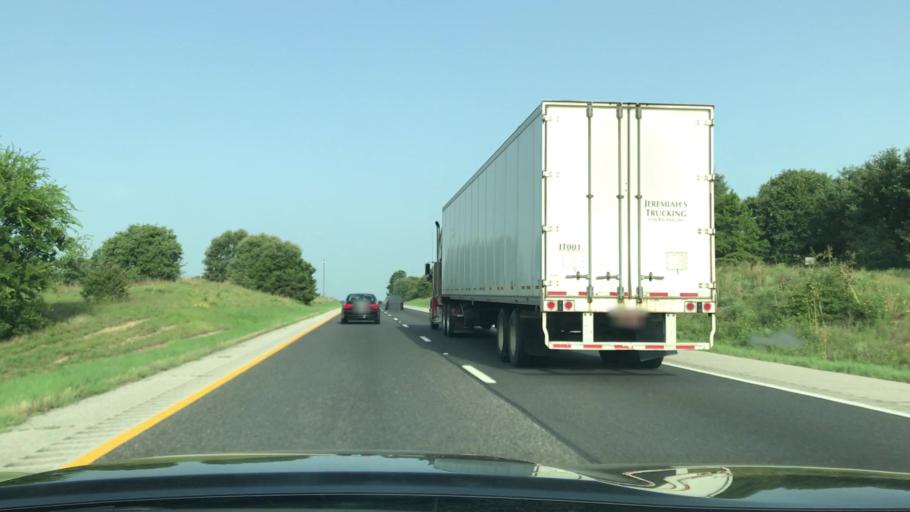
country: US
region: Texas
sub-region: Smith County
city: Tyler
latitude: 32.4524
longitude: -95.2658
